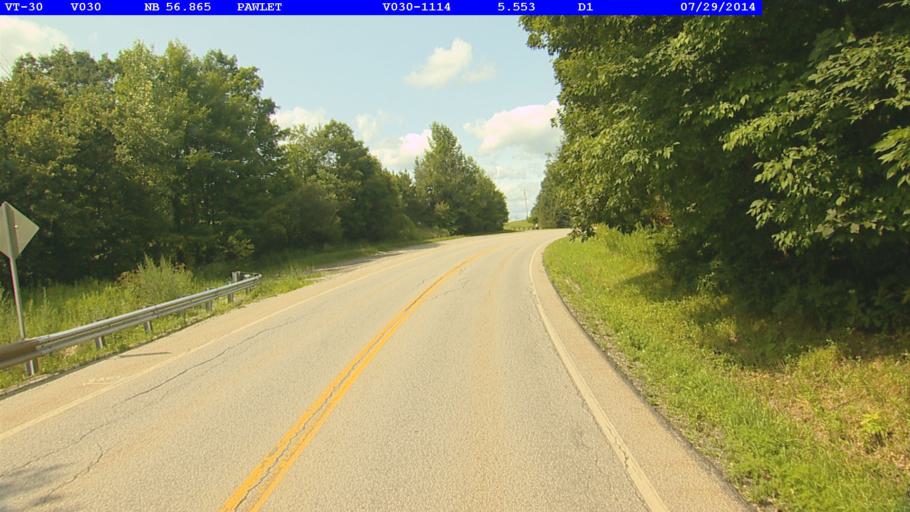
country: US
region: New York
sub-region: Washington County
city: Granville
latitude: 43.3776
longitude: -73.2050
